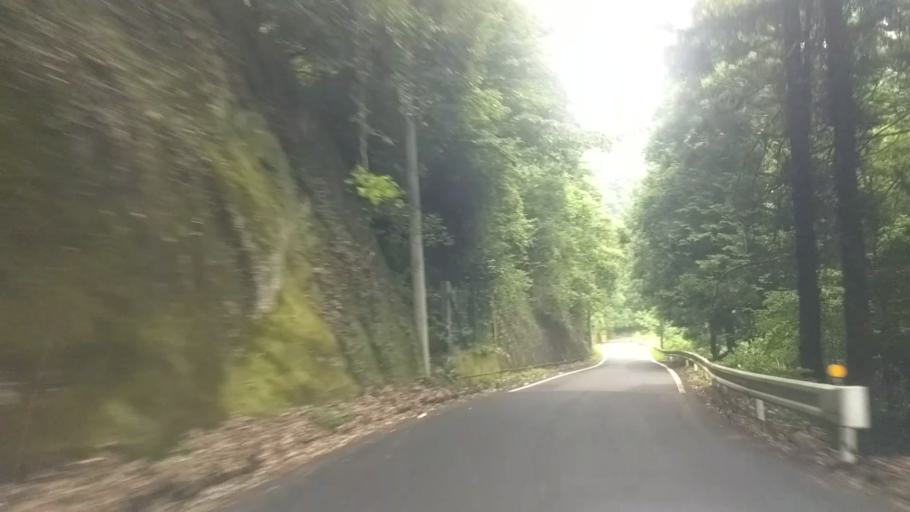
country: JP
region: Chiba
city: Kawaguchi
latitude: 35.2237
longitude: 140.1445
